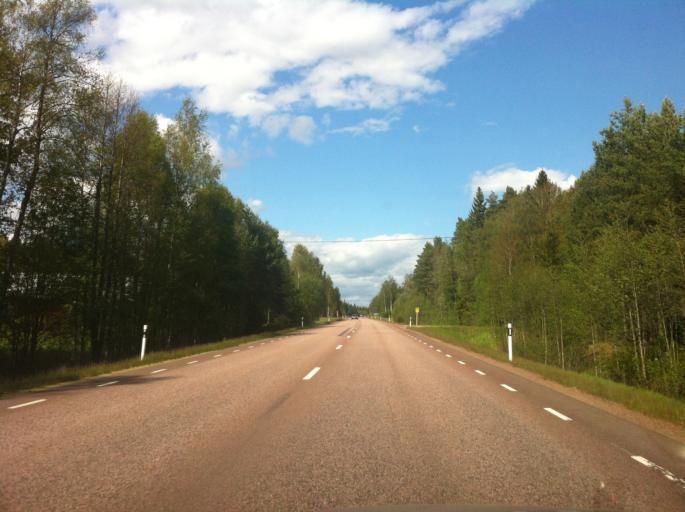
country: SE
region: Vaermland
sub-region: Kristinehamns Kommun
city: Kristinehamn
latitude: 59.3733
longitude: 14.1695
